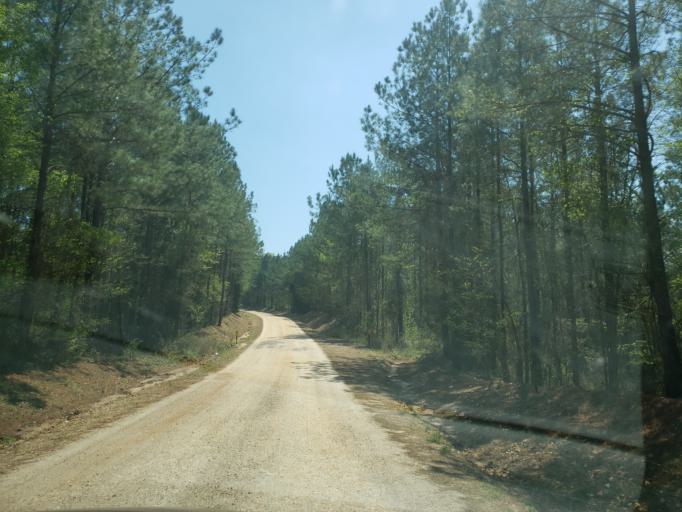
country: US
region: Alabama
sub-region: Tallapoosa County
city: Camp Hill
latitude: 32.6536
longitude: -85.6576
